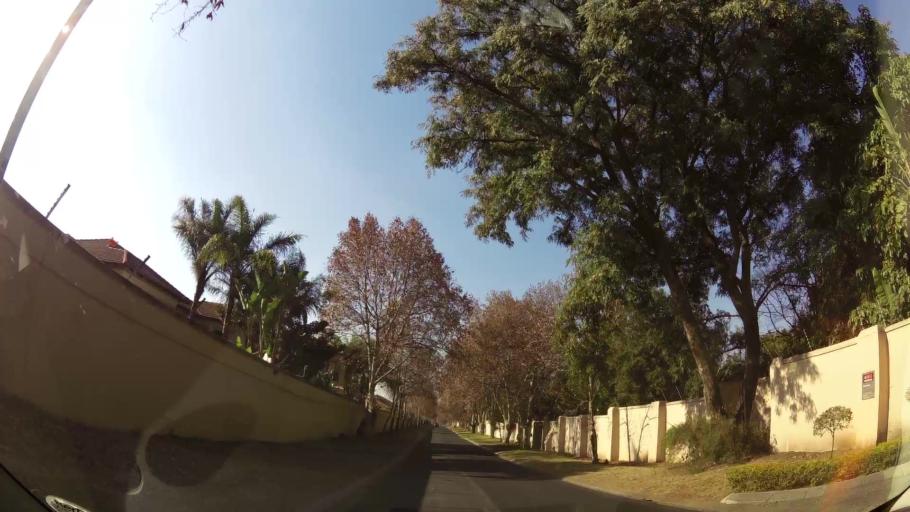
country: ZA
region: Gauteng
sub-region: City of Johannesburg Metropolitan Municipality
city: Diepsloot
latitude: -26.0667
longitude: 28.0013
